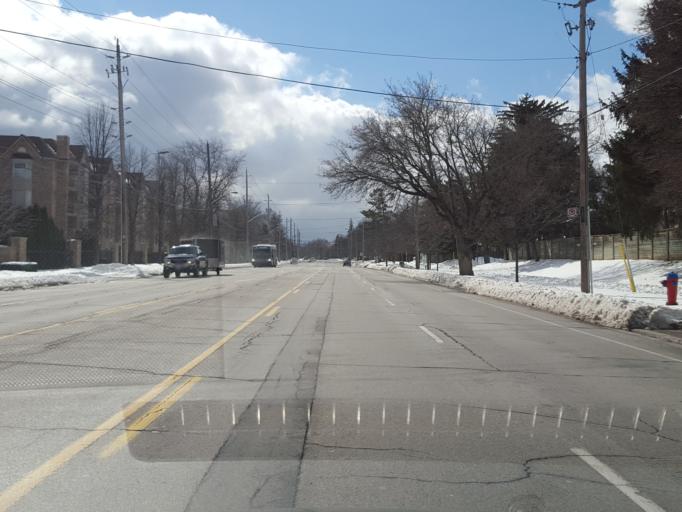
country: CA
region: Ontario
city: Hamilton
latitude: 43.3017
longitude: -79.8593
